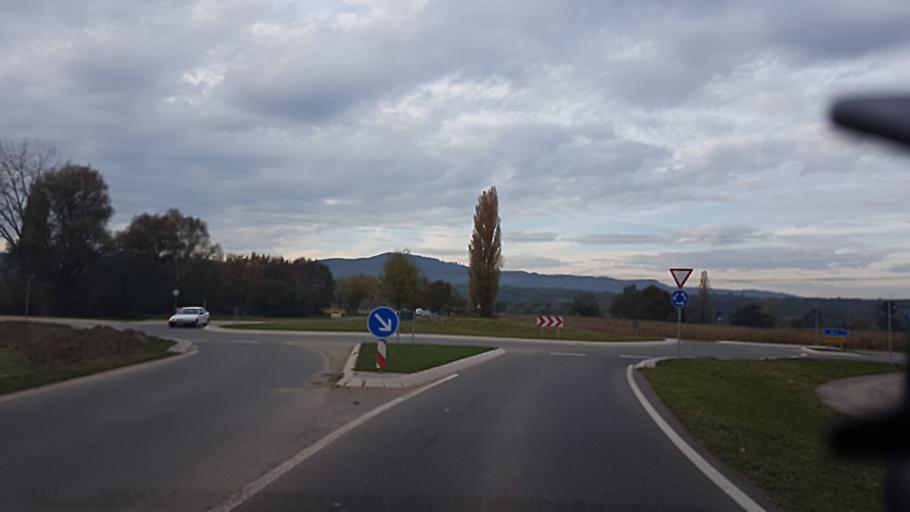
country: DE
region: Baden-Wuerttemberg
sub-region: Freiburg Region
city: Botzingen
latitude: 48.0708
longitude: 7.7446
